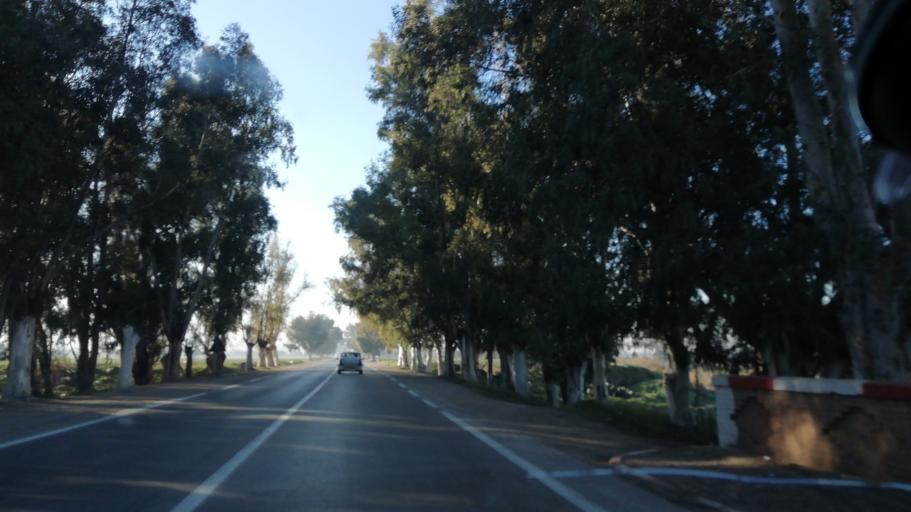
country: DZ
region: Tlemcen
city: Remchi
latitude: 35.0527
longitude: -1.5020
